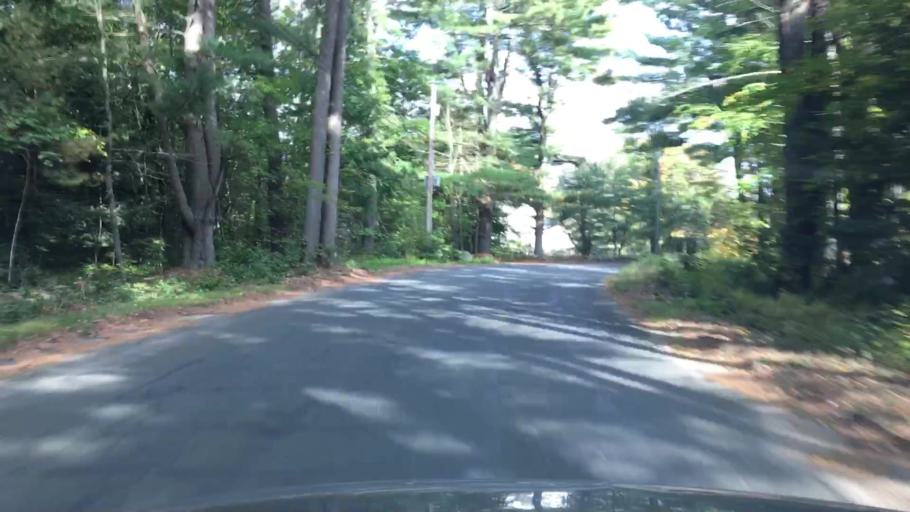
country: US
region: Connecticut
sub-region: Tolland County
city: Stafford
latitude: 41.9953
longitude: -72.3251
